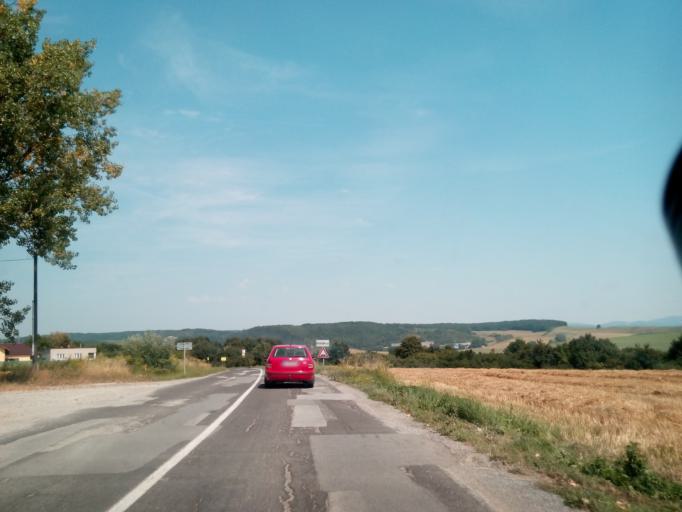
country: SK
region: Kosicky
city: Kosice
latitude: 48.7898
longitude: 21.2441
